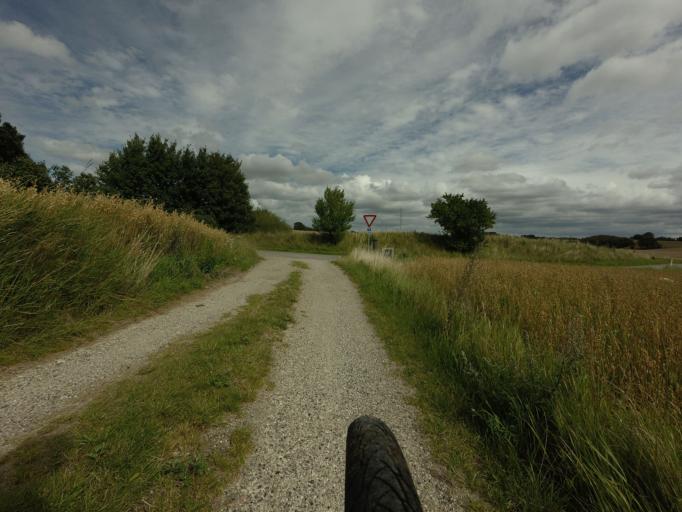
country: DK
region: Central Jutland
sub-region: Syddjurs Kommune
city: Ryomgard
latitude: 56.4040
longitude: 10.5397
